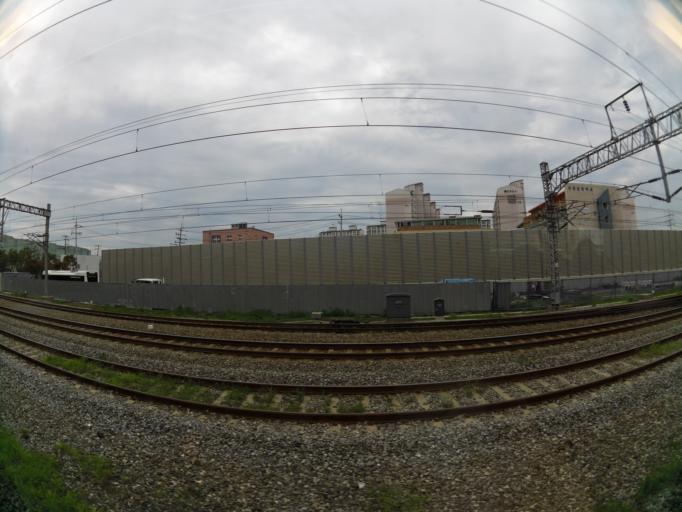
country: KR
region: Gyeonggi-do
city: Suwon-si
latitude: 37.2683
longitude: 126.9983
